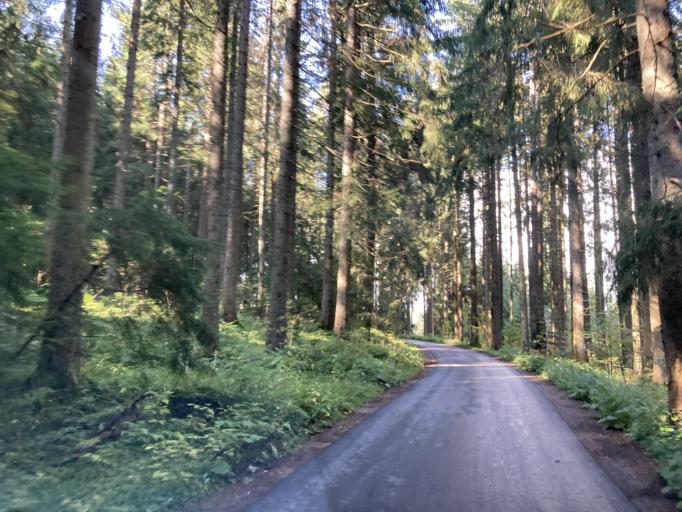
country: DE
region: Baden-Wuerttemberg
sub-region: Freiburg Region
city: Vohrenbach
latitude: 48.0952
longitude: 8.2817
